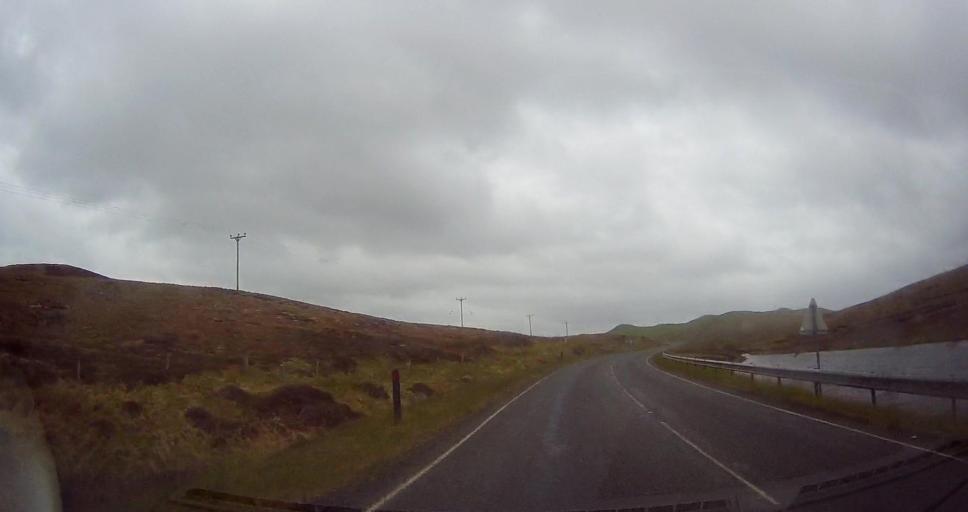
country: GB
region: Scotland
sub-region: Shetland Islands
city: Lerwick
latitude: 60.4374
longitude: -1.3972
